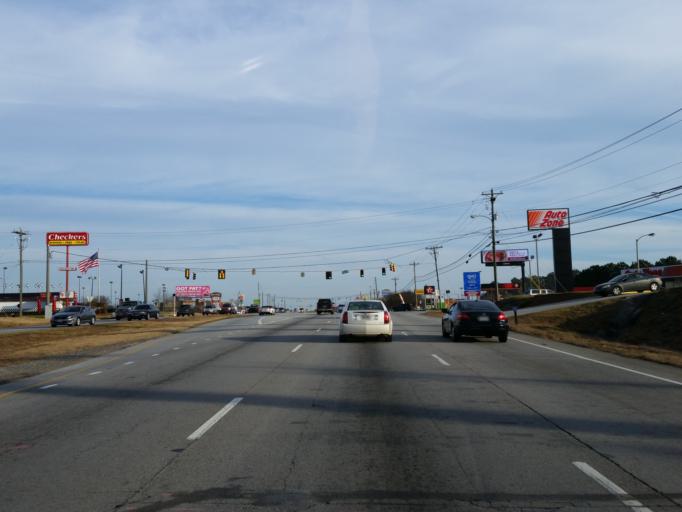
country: US
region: Georgia
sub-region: Paulding County
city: Hiram
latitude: 33.8936
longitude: -84.7611
